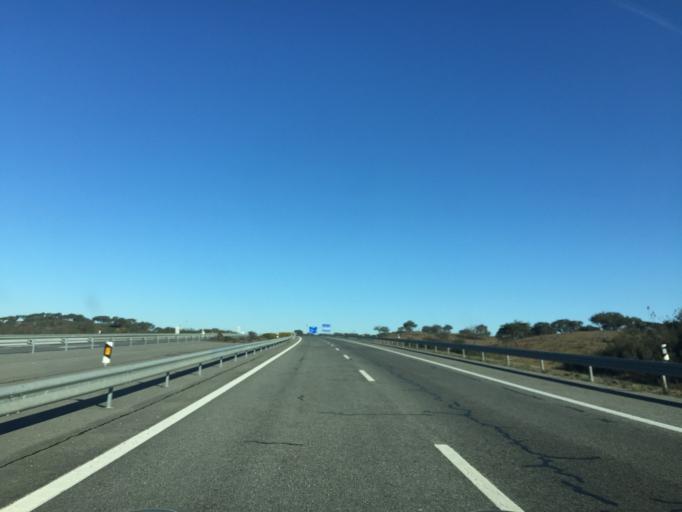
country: PT
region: Beja
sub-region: Almodovar
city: Almodovar
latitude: 37.5274
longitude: -8.1815
